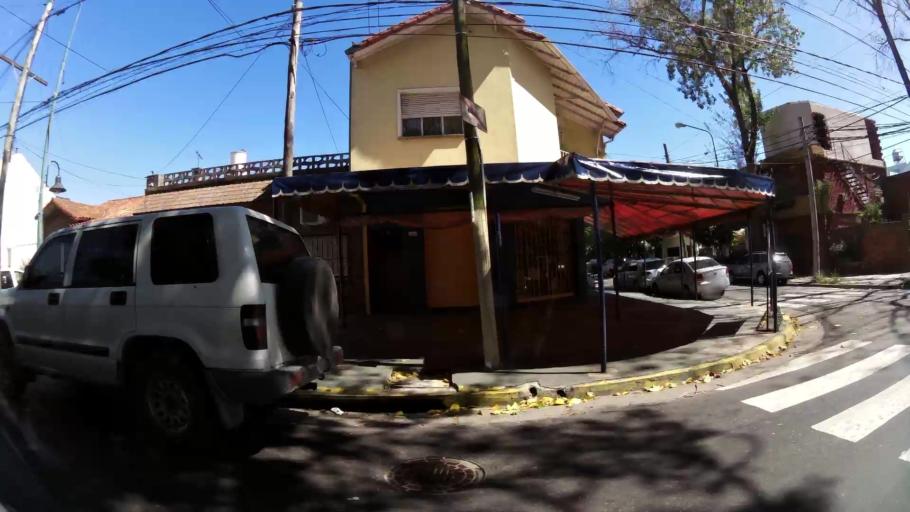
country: AR
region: Buenos Aires
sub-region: Partido de Vicente Lopez
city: Olivos
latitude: -34.5196
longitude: -58.5170
